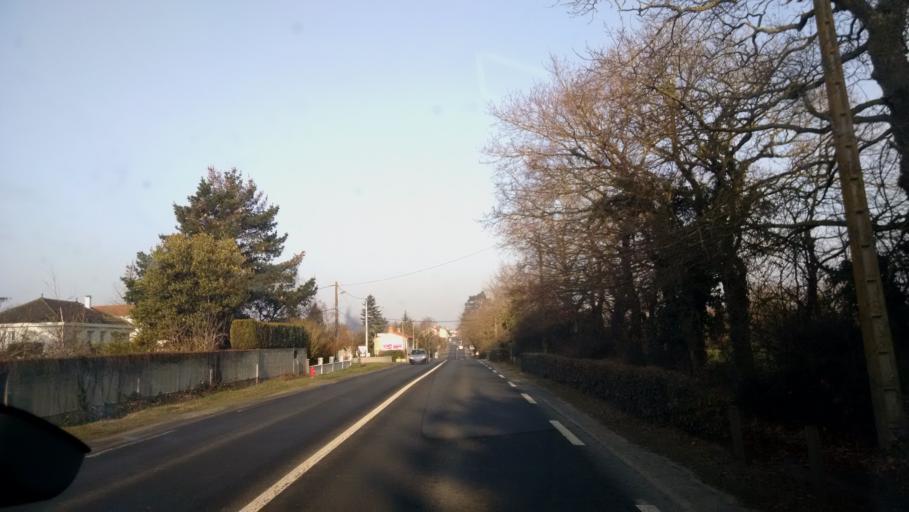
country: FR
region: Pays de la Loire
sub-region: Departement de la Loire-Atlantique
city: Aigrefeuille-sur-Maine
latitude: 47.0727
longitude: -1.3937
